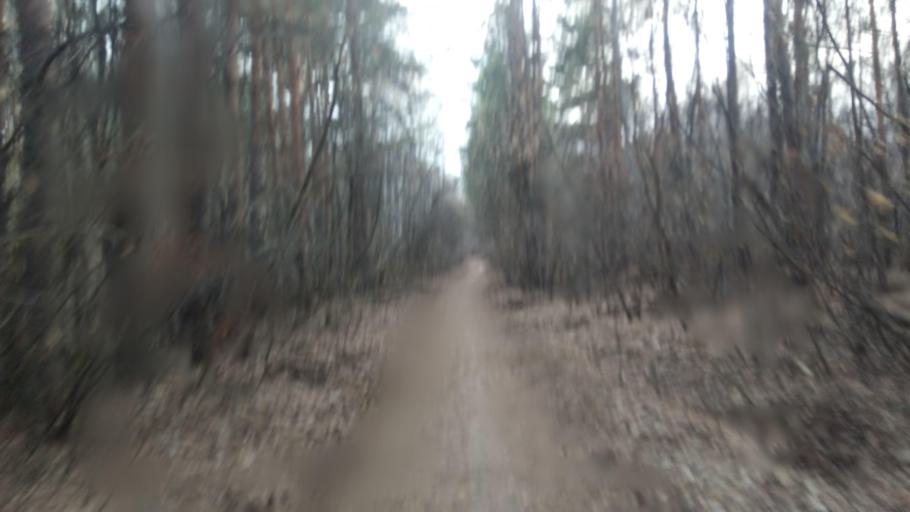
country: RU
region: Chelyabinsk
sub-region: Gorod Chelyabinsk
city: Chelyabinsk
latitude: 55.1454
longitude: 61.3482
